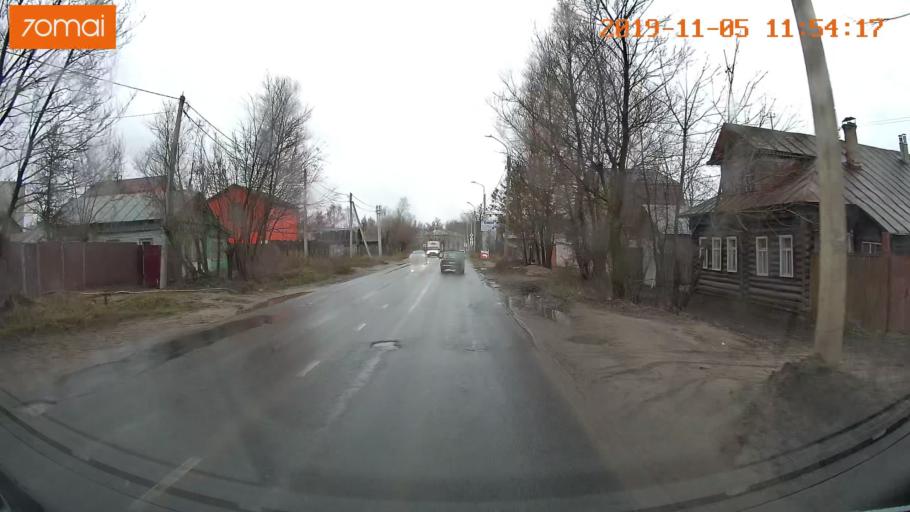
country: RU
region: Ivanovo
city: Bogorodskoye
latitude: 56.9915
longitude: 41.0312
